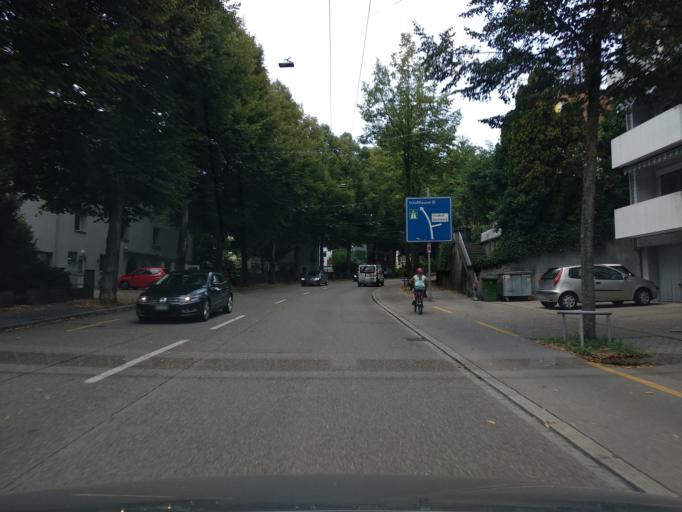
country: CH
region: Zurich
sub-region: Bezirk Winterthur
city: Veltheim
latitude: 47.5118
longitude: 8.7216
